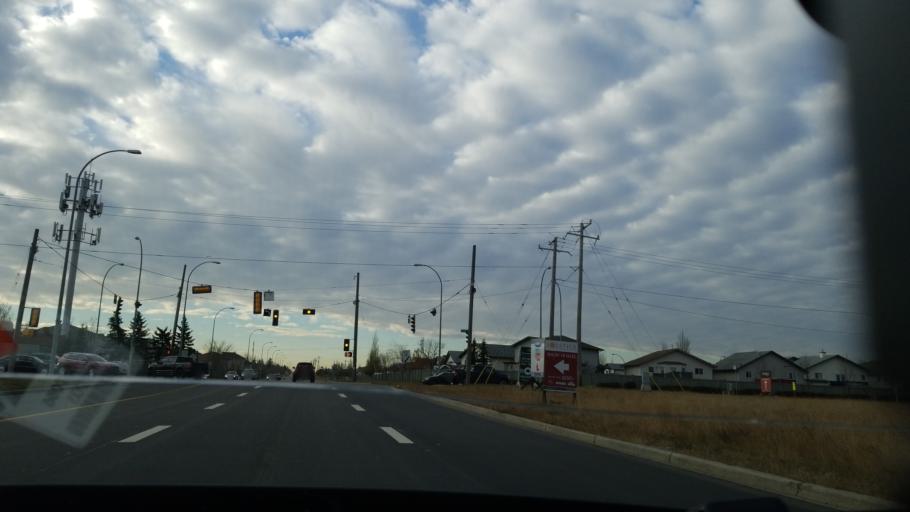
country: CA
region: Alberta
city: Edmonton
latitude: 53.6292
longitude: -113.4429
